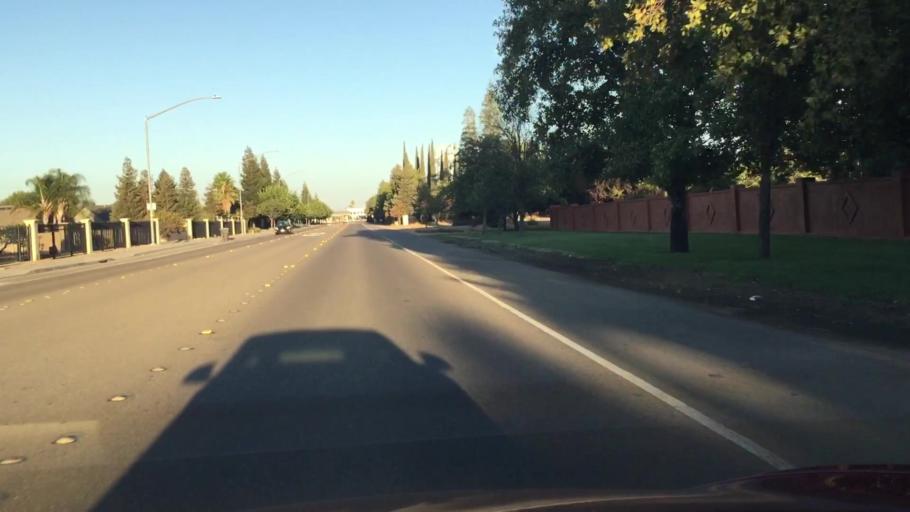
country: US
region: California
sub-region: San Joaquin County
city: Tracy
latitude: 37.7107
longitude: -121.4033
